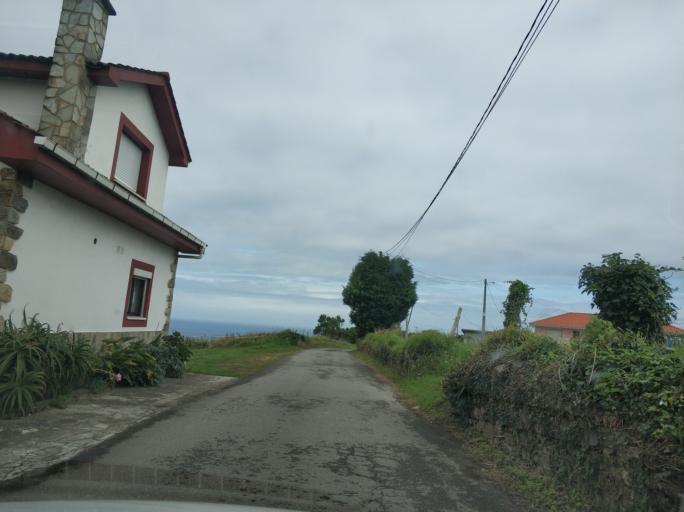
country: ES
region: Asturias
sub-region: Province of Asturias
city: Cudillero
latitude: 43.5613
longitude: -6.2973
